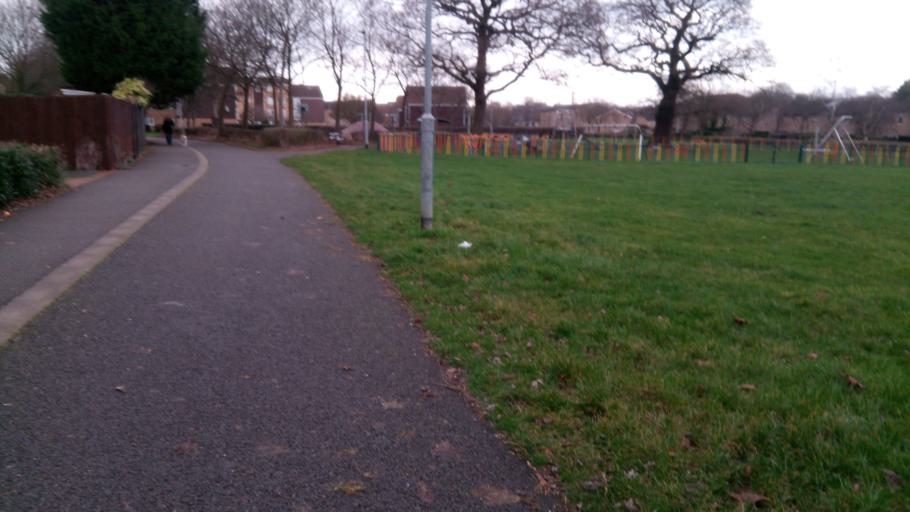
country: GB
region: England
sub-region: Peterborough
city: Marholm
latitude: 52.5795
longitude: -0.2869
